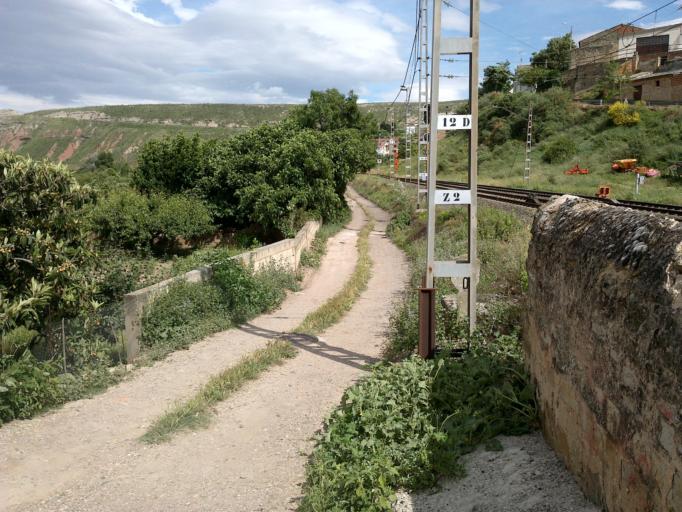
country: ES
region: La Rioja
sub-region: Provincia de La Rioja
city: Alcanadre
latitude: 42.4074
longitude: -2.1208
